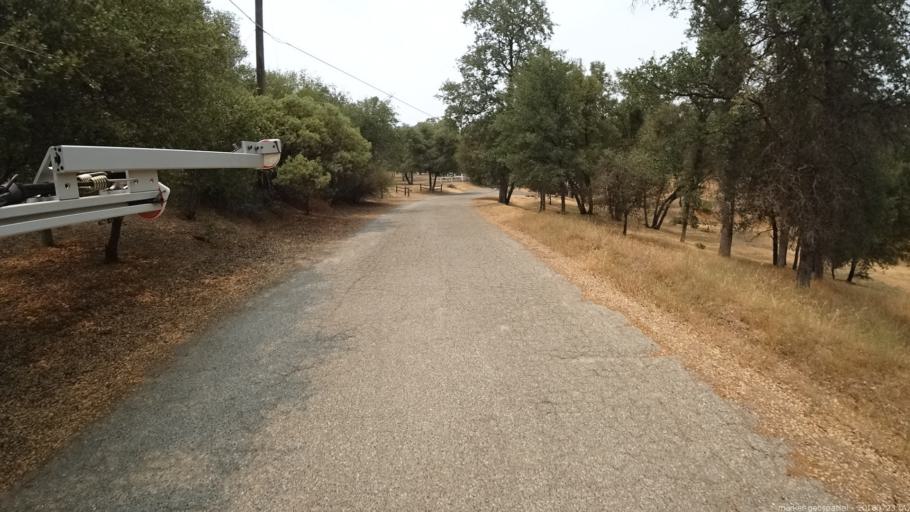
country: US
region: California
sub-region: Madera County
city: Oakhurst
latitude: 37.3416
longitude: -119.6468
